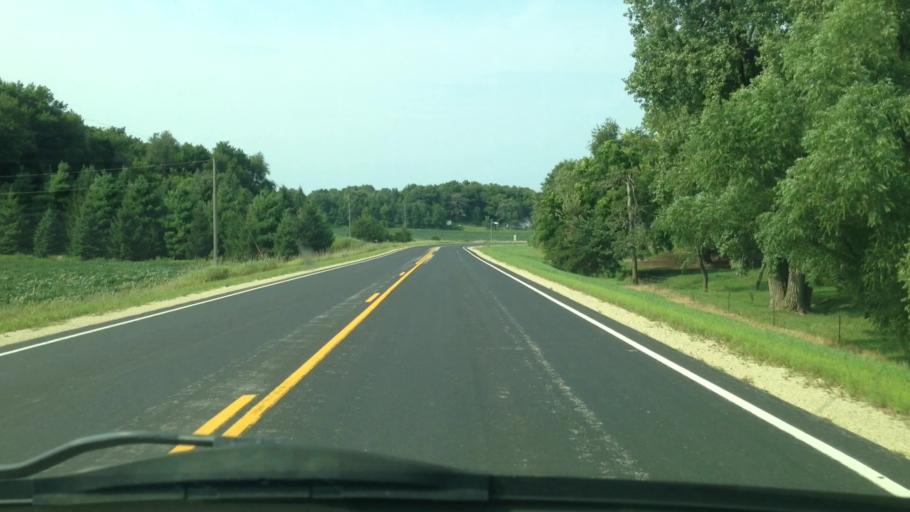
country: US
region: Minnesota
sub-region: Winona County
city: Lewiston
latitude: 43.9643
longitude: -91.9543
